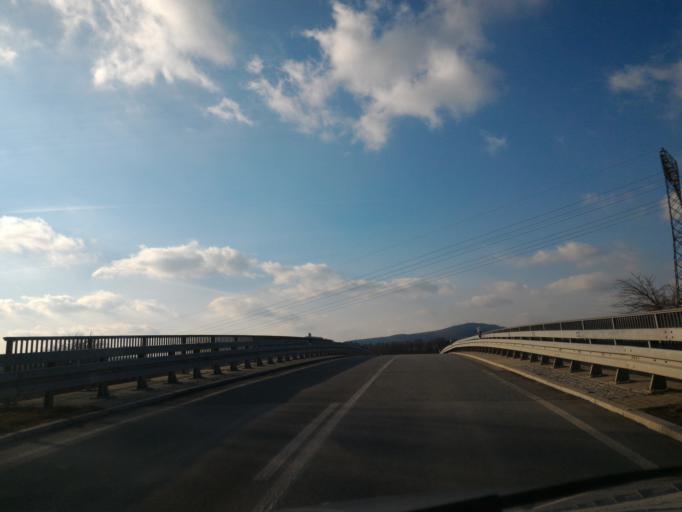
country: DE
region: Saxony
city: Grossschonau
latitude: 50.8907
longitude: 14.6883
